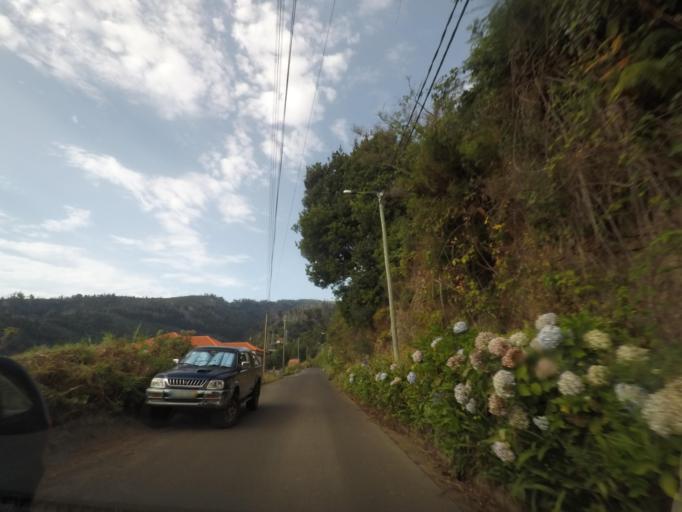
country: PT
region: Madeira
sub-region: Calheta
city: Arco da Calheta
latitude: 32.7336
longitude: -17.1546
